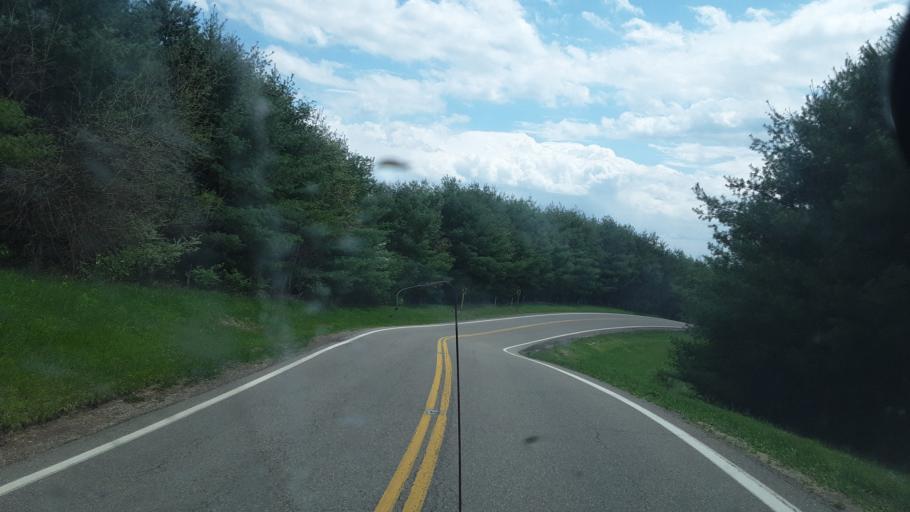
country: US
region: Ohio
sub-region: Noble County
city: Caldwell
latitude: 39.7275
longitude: -81.6523
